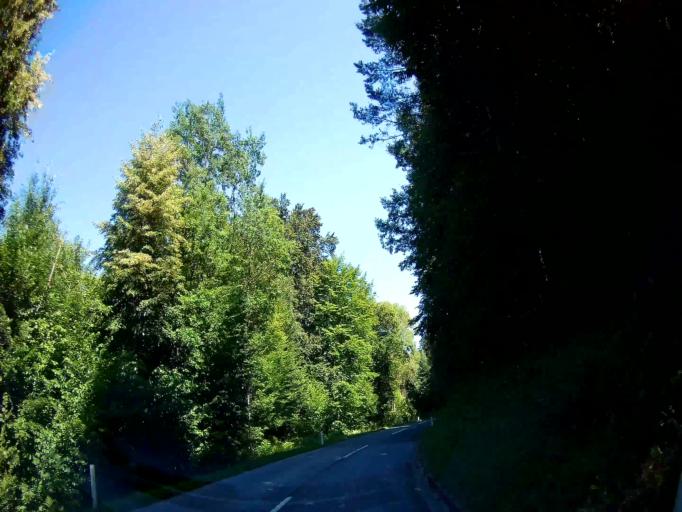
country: AT
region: Carinthia
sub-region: Politischer Bezirk Klagenfurt Land
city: Grafenstein
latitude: 46.6014
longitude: 14.4292
